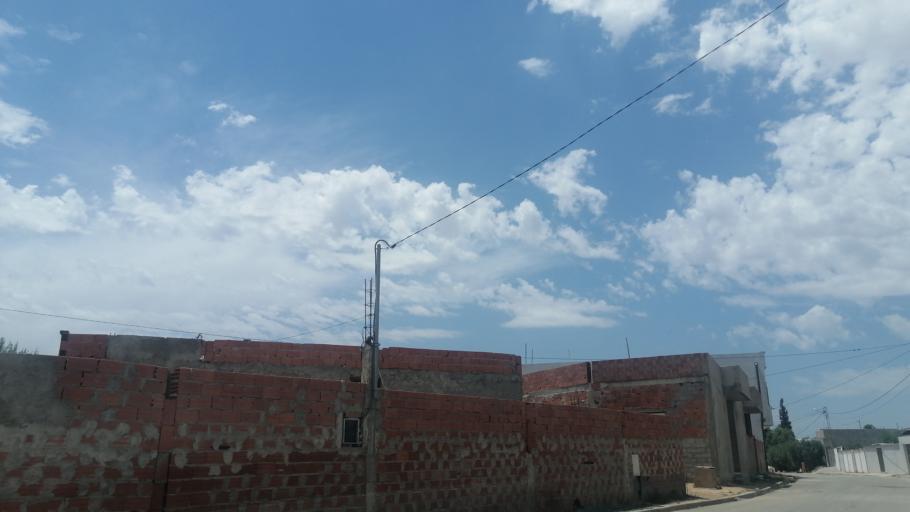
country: TN
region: Al Qayrawan
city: Sbikha
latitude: 36.1275
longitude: 10.0950
